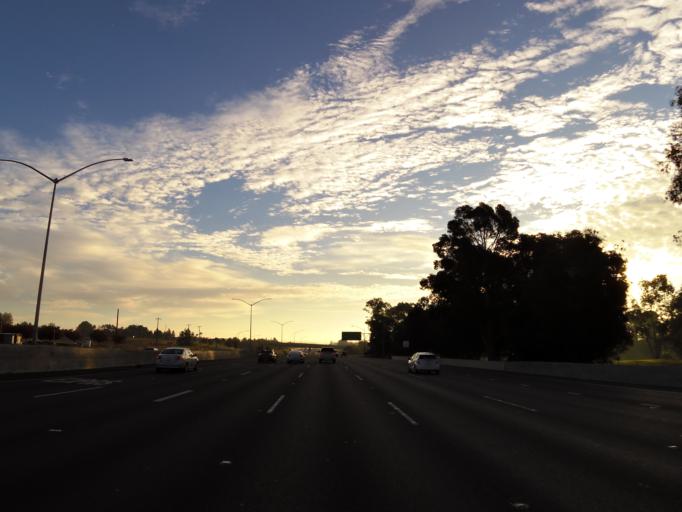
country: US
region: California
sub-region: Alameda County
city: Livermore
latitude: 37.7009
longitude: -121.8241
